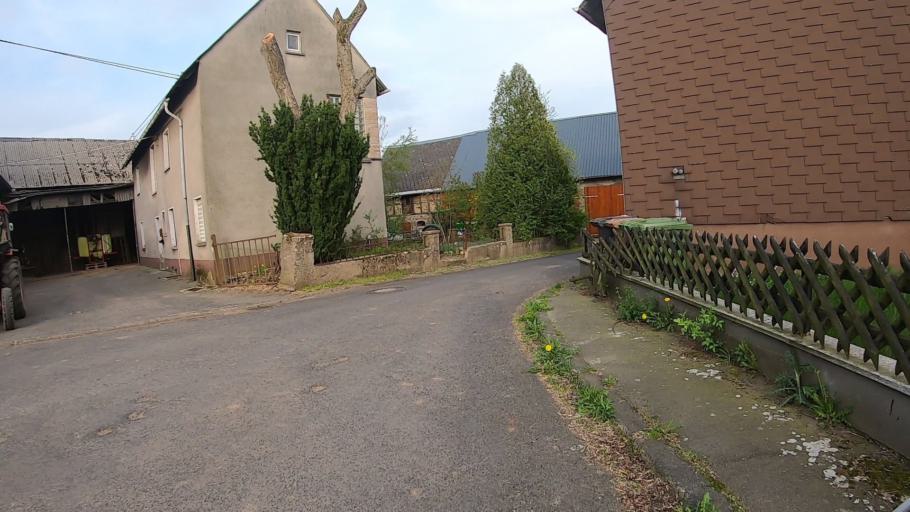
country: DE
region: Rheinland-Pfalz
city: Weidenhahn
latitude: 50.5436
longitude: 7.8308
